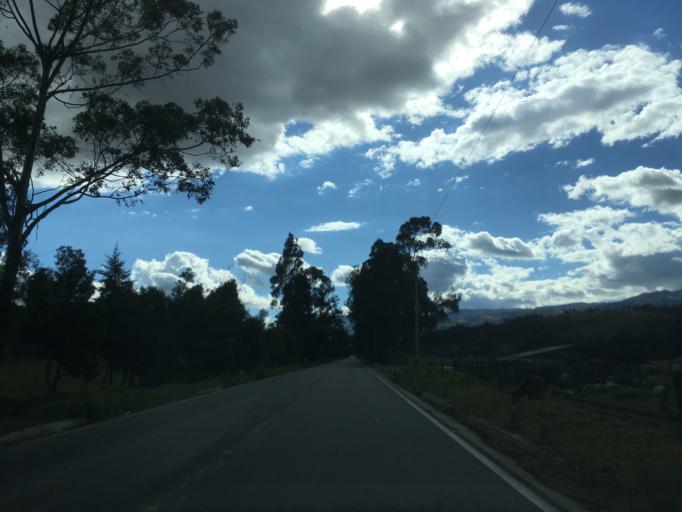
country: CO
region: Boyaca
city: Firavitoba
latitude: 5.6379
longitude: -72.9962
